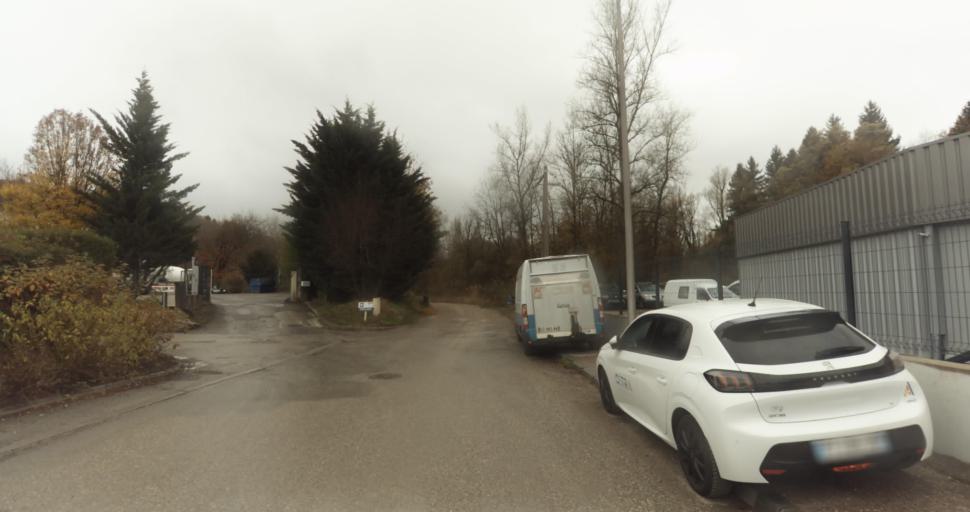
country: FR
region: Rhone-Alpes
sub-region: Departement de la Haute-Savoie
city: Saint-Martin-Bellevue
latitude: 45.9520
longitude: 6.1663
